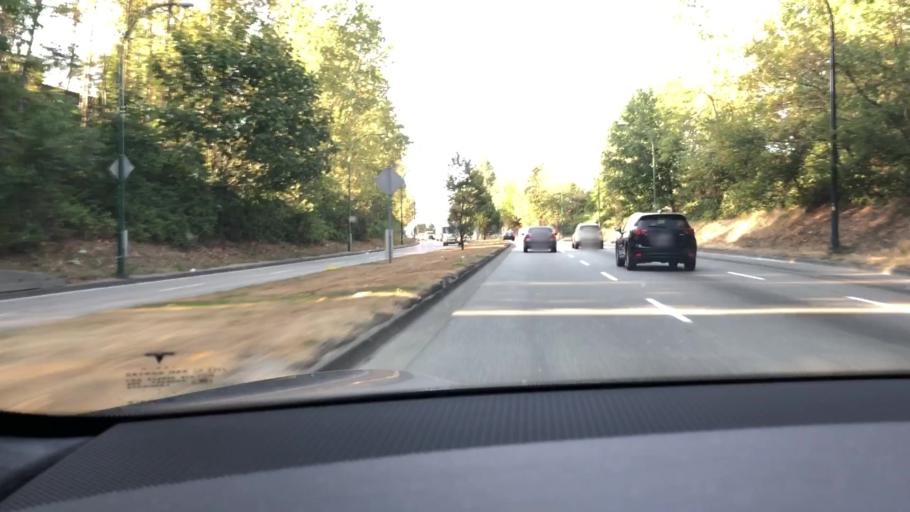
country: CA
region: British Columbia
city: Burnaby
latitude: 49.2111
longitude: -123.0238
